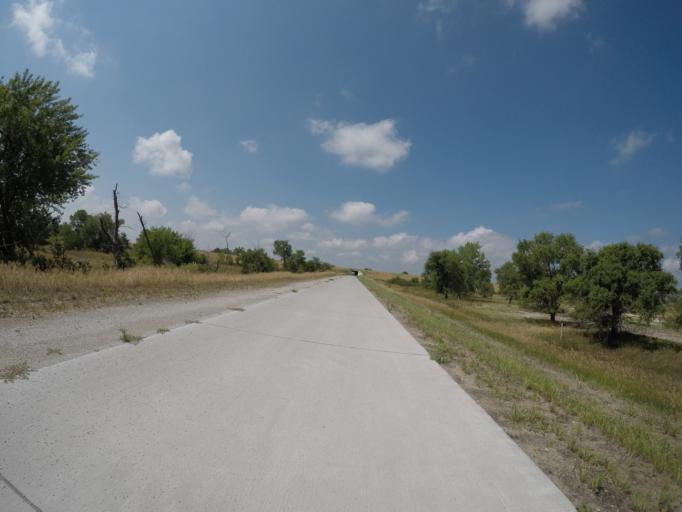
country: US
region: Nebraska
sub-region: Buffalo County
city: Kearney
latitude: 40.6773
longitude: -98.9920
